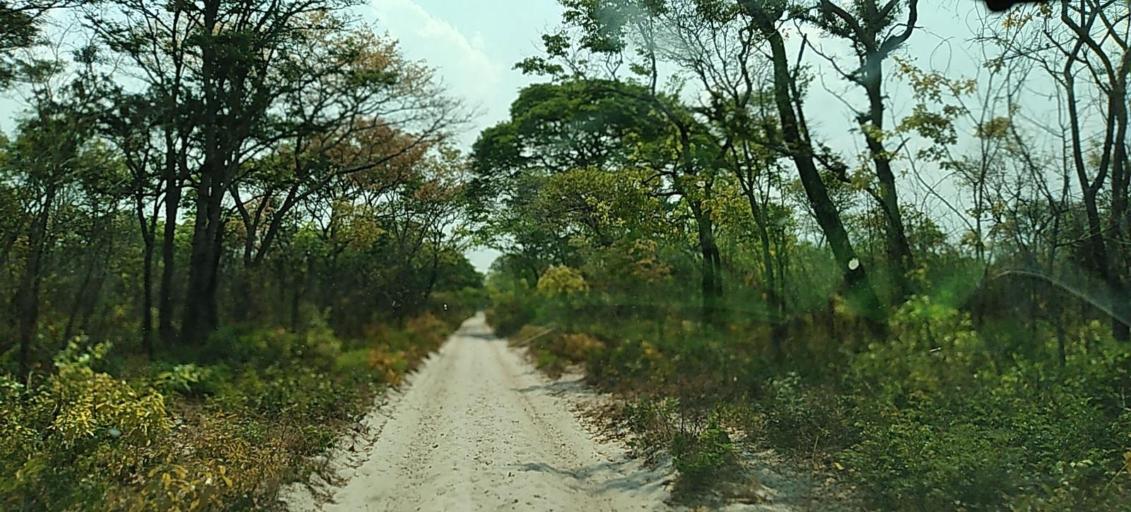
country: ZM
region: North-Western
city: Kabompo
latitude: -13.3882
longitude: 23.7761
